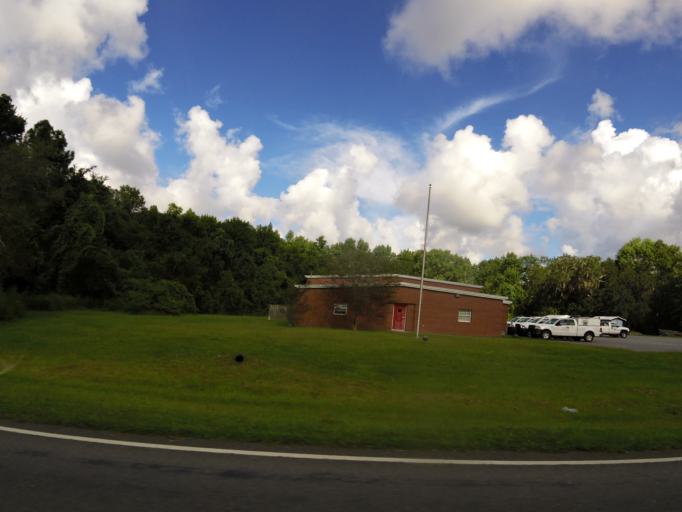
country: US
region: Georgia
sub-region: Camden County
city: Kingsland
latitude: 30.8451
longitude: -81.6992
